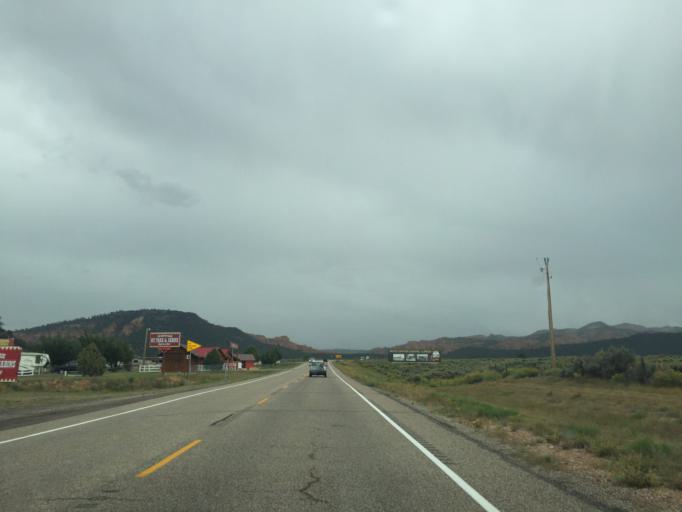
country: US
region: Utah
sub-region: Garfield County
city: Panguitch
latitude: 37.7487
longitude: -112.3635
